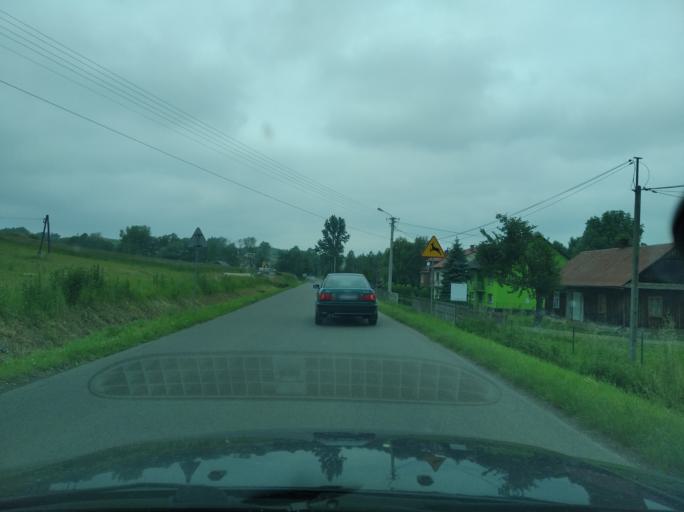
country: PL
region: Subcarpathian Voivodeship
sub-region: Powiat ropczycko-sedziszowski
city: Sedziszow Malopolski
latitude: 50.0442
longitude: 21.7003
